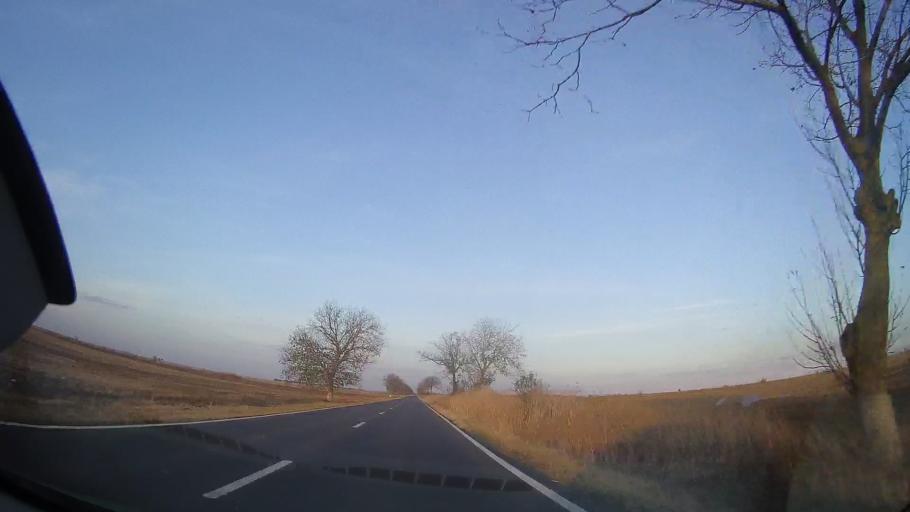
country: RO
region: Constanta
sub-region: Comuna Topraisar
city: Topraisar
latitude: 43.9919
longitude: 28.4259
